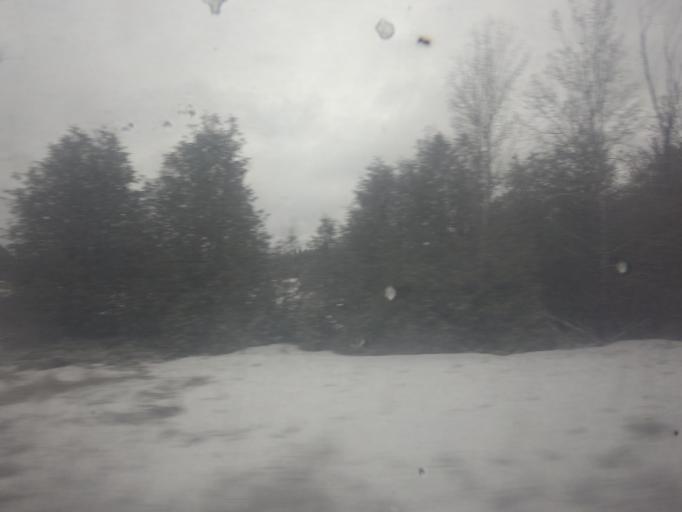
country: CA
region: Ontario
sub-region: Lanark County
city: Smiths Falls
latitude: 44.9979
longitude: -75.9657
